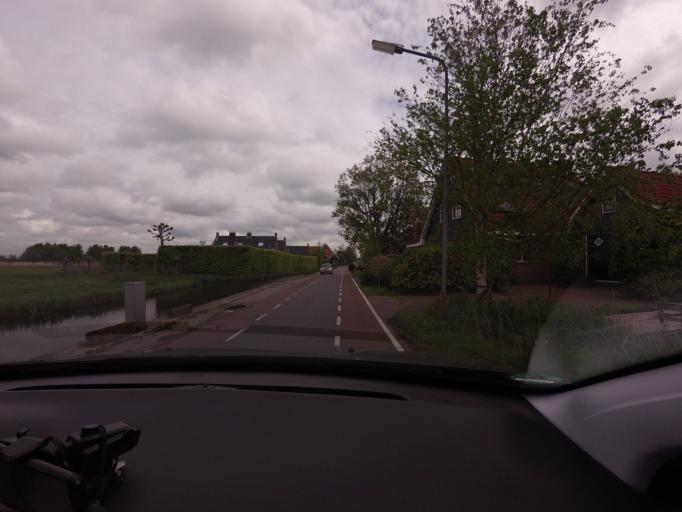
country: NL
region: North Holland
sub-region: Gemeente Landsmeer
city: Landsmeer
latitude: 52.4650
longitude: 4.8869
